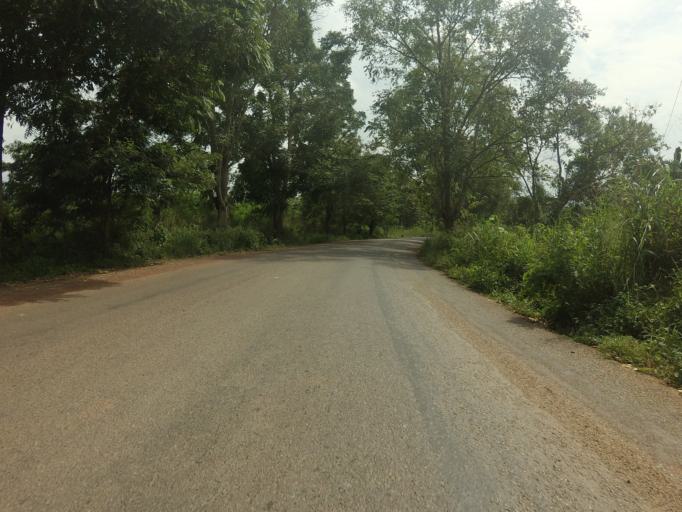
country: GH
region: Eastern
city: Aburi
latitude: 5.9666
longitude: -0.2190
